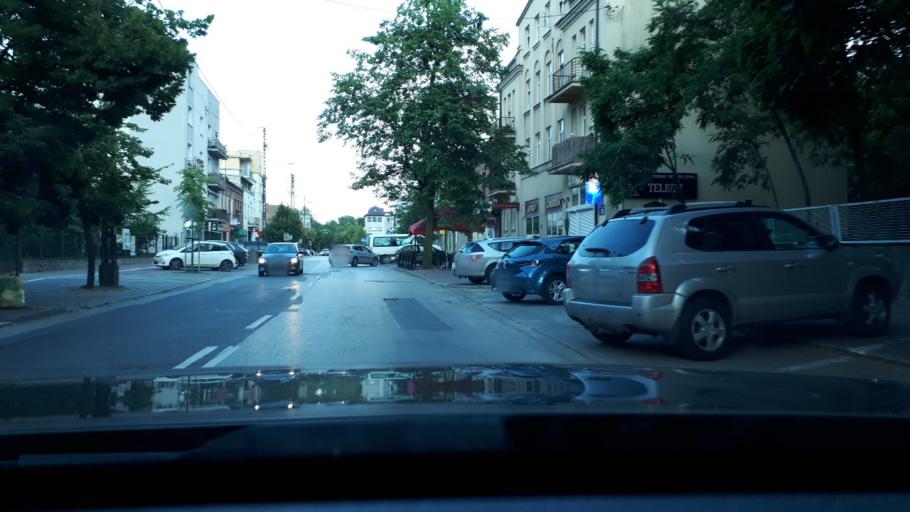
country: PL
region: Masovian Voivodeship
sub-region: Powiat pruszkowski
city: Pruszkow
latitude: 52.1666
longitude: 20.8031
